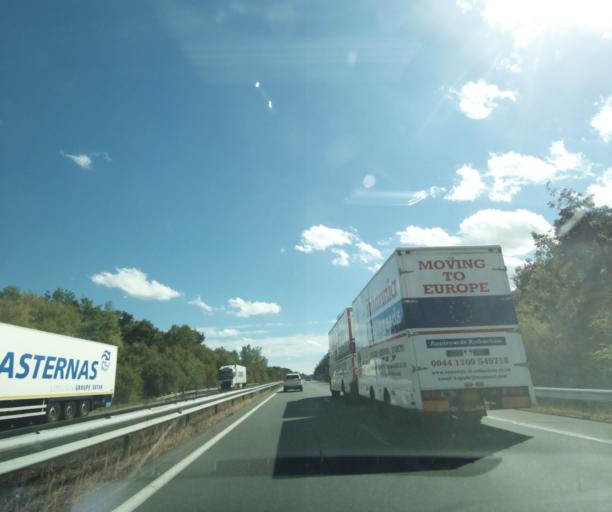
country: FR
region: Aquitaine
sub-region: Departement du Lot-et-Garonne
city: Fourques-sur-Garonne
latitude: 44.4131
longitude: 0.1793
